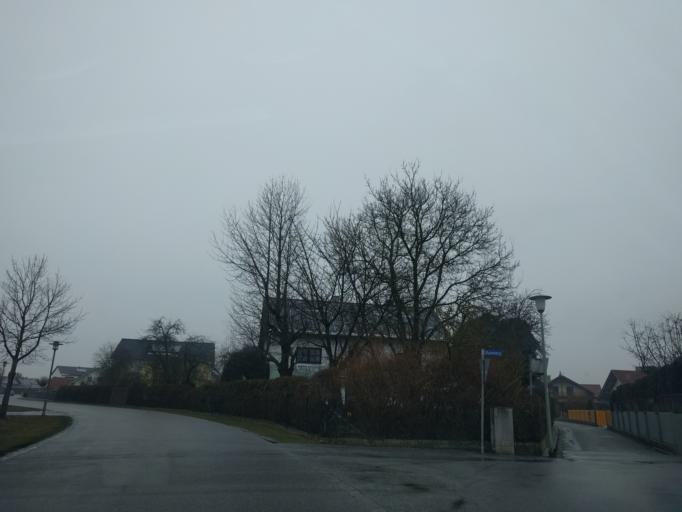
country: DE
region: Bavaria
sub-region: Lower Bavaria
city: Osterhofen
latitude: 48.7031
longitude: 13.0286
